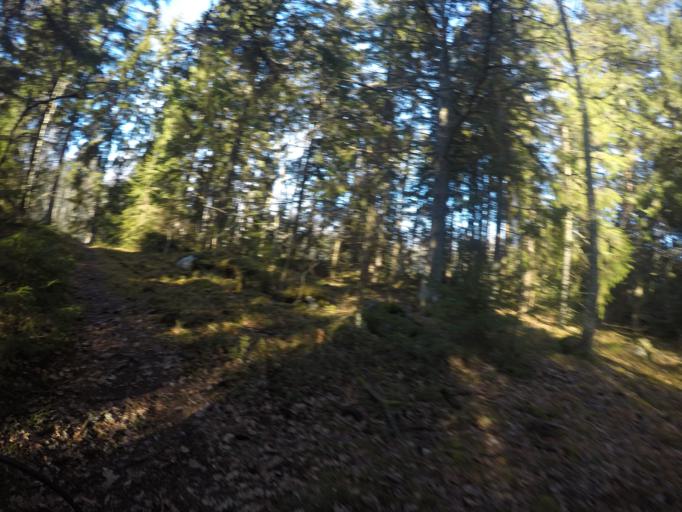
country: SE
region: Soedermanland
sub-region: Eskilstuna Kommun
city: Kvicksund
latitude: 59.4477
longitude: 16.3628
